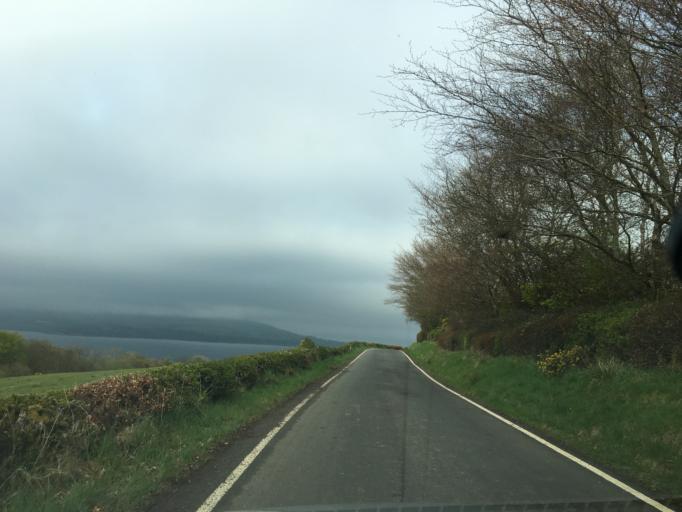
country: GB
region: Scotland
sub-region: Argyll and Bute
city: Rothesay
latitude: 55.8372
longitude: -5.0376
